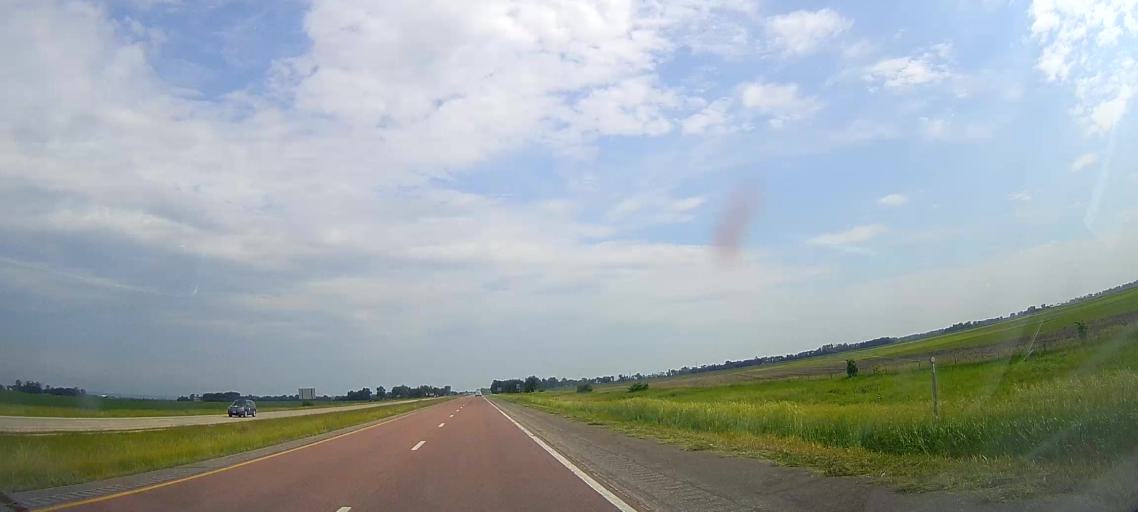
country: US
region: Iowa
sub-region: Monona County
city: Onawa
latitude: 42.0054
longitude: -96.1160
